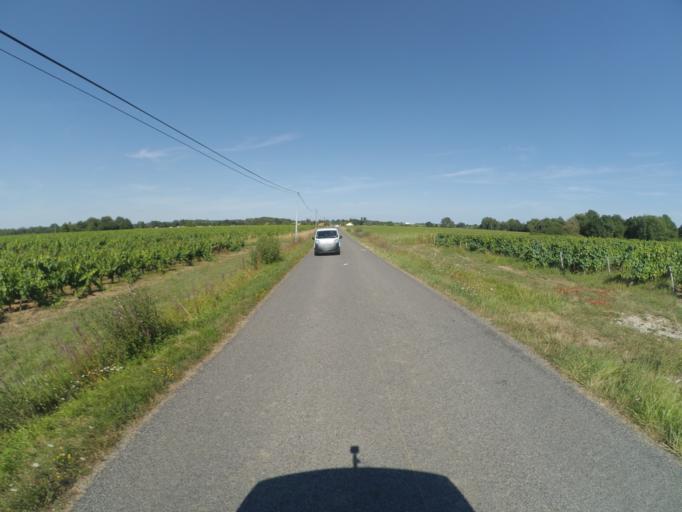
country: FR
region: Pays de la Loire
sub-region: Departement de la Loire-Atlantique
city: Le Pallet
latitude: 47.1581
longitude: -1.3123
